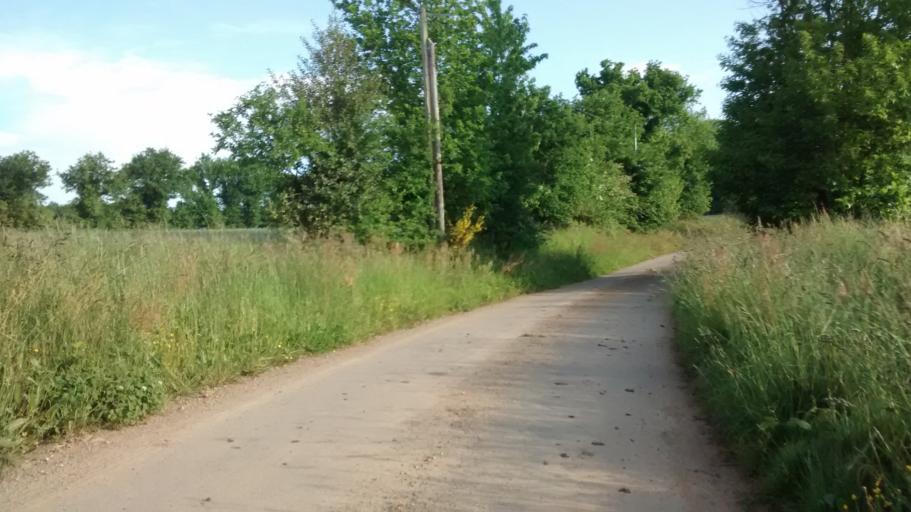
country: FR
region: Brittany
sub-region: Departement du Morbihan
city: Malestroit
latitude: 47.7970
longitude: -2.4011
